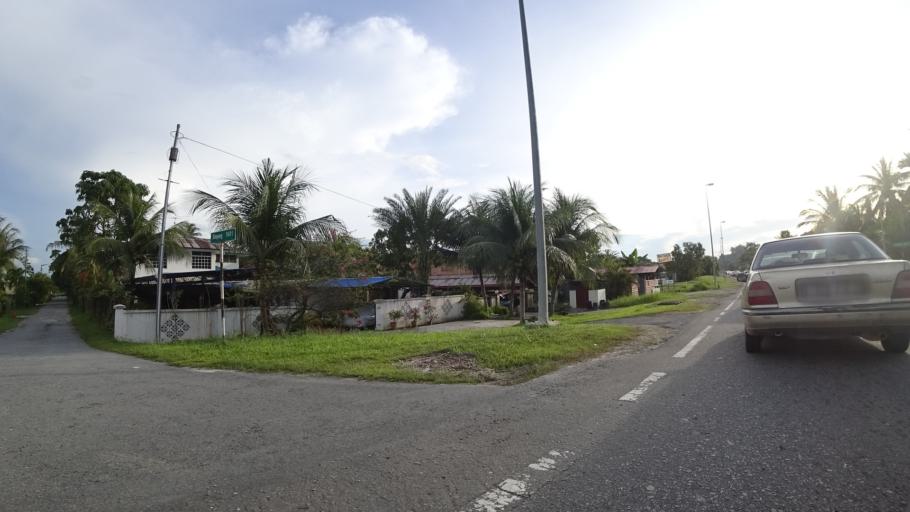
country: BN
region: Brunei and Muara
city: Bandar Seri Begawan
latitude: 4.8835
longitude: 114.8356
